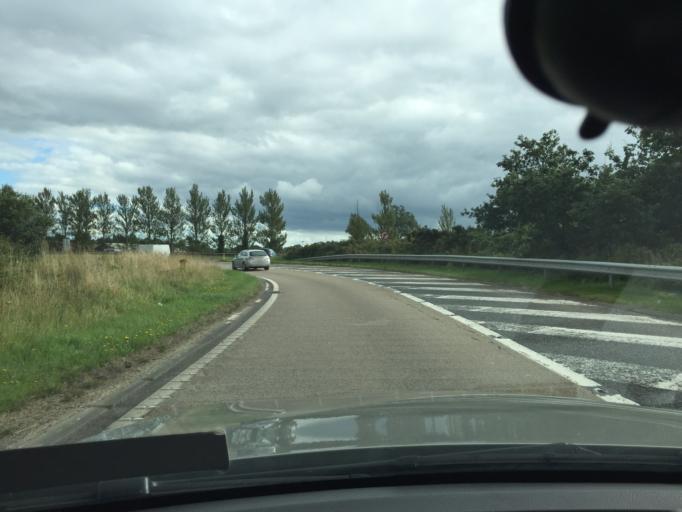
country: GB
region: Northern Ireland
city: Hillsborough
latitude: 54.4947
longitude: -6.0603
